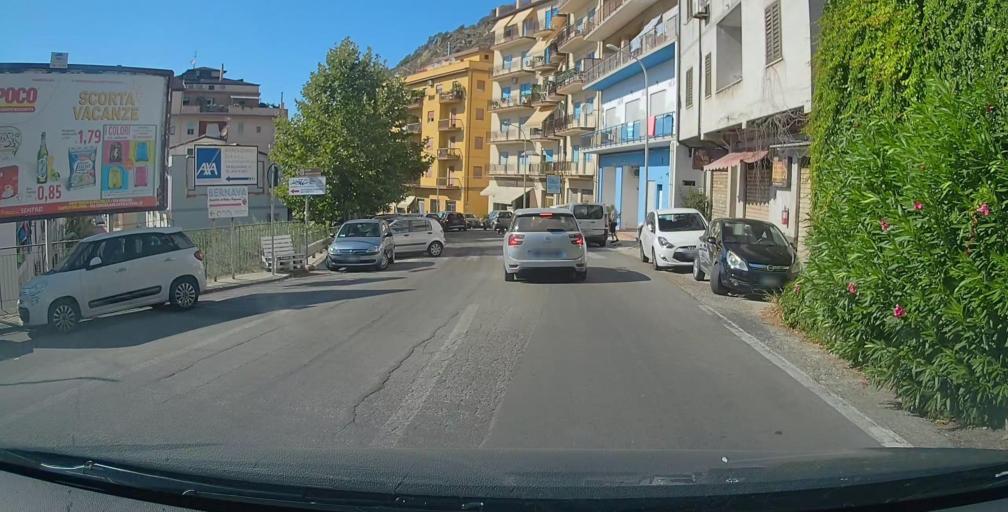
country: IT
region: Sicily
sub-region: Messina
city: Capo d'Orlando
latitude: 38.1619
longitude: 14.7488
